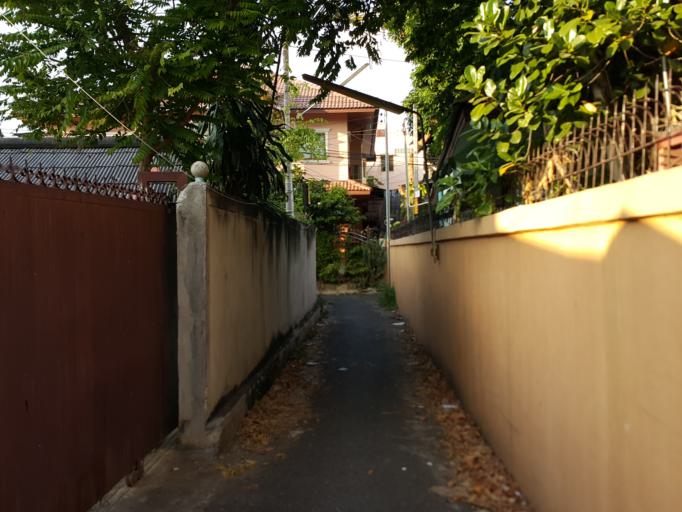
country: TH
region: Chiang Mai
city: Chiang Mai
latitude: 18.7838
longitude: 98.9899
